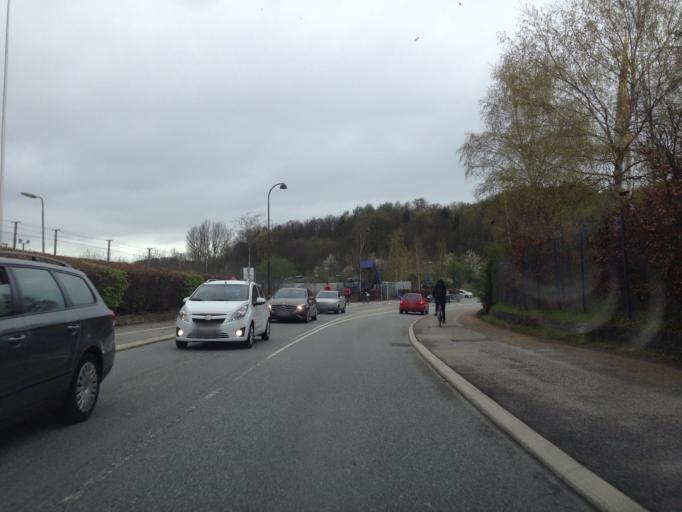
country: DK
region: Capital Region
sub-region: Rudersdal Kommune
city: Trorod
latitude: 55.8181
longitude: 12.5284
